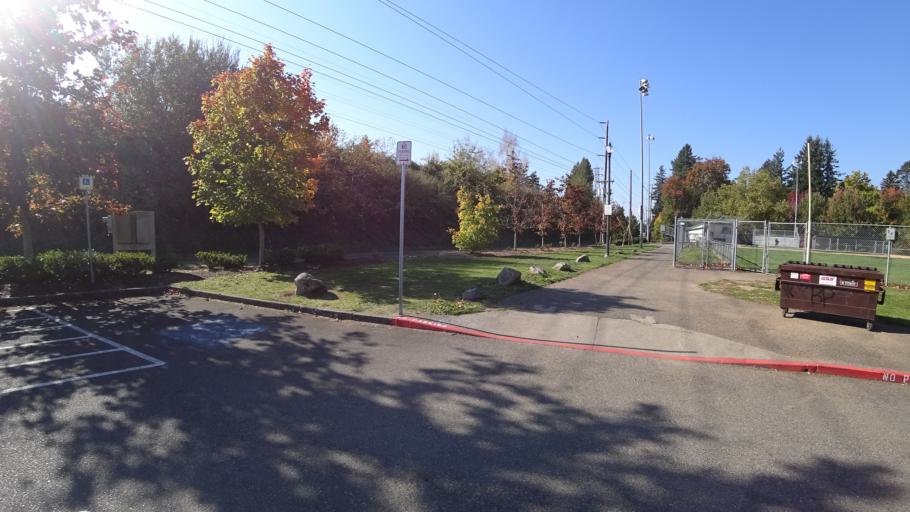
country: US
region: Oregon
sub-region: Multnomah County
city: Gresham
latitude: 45.4956
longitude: -122.4316
